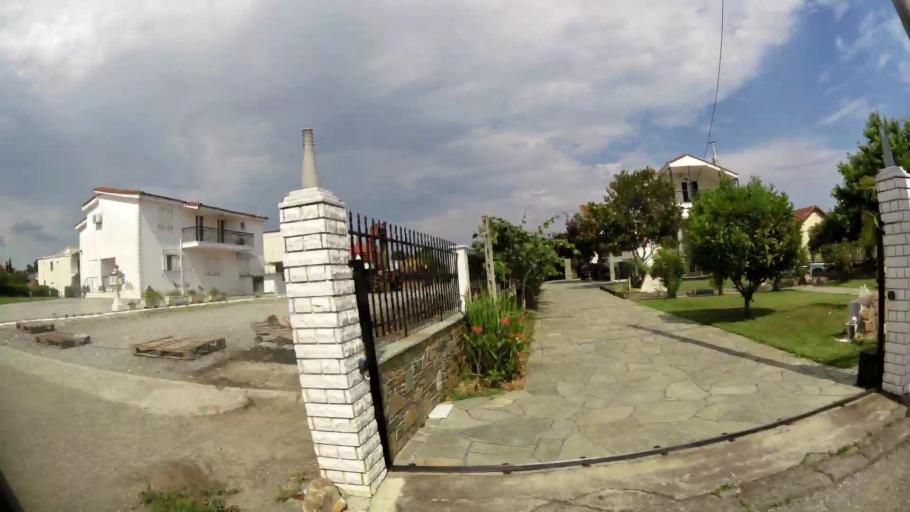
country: GR
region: Central Macedonia
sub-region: Nomos Pierias
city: Makrygialos
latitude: 40.4125
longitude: 22.6043
